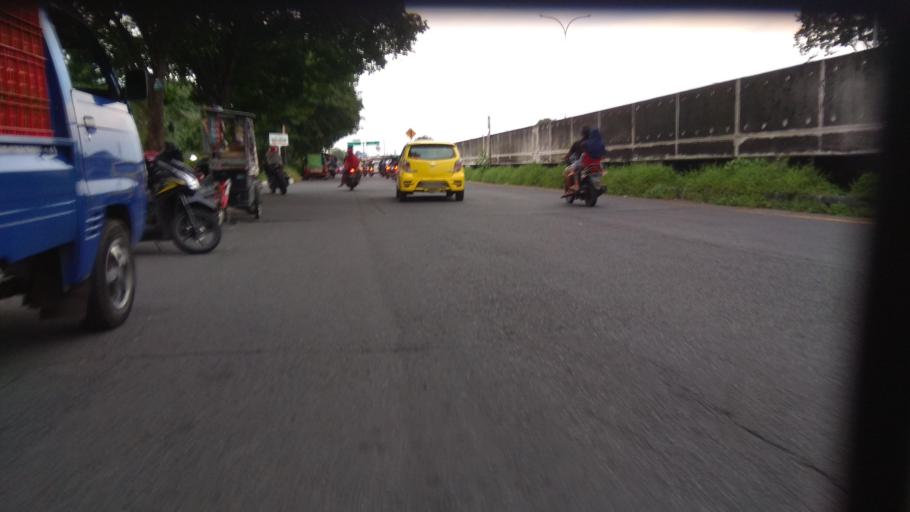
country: ID
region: East Java
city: Tambaksumur
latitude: -7.3439
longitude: 112.7751
